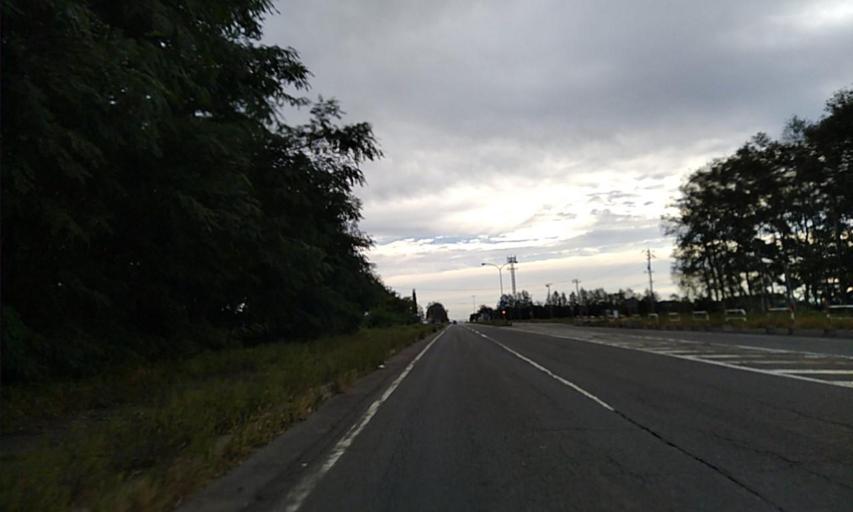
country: JP
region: Hokkaido
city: Obihiro
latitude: 42.9184
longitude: 143.0151
